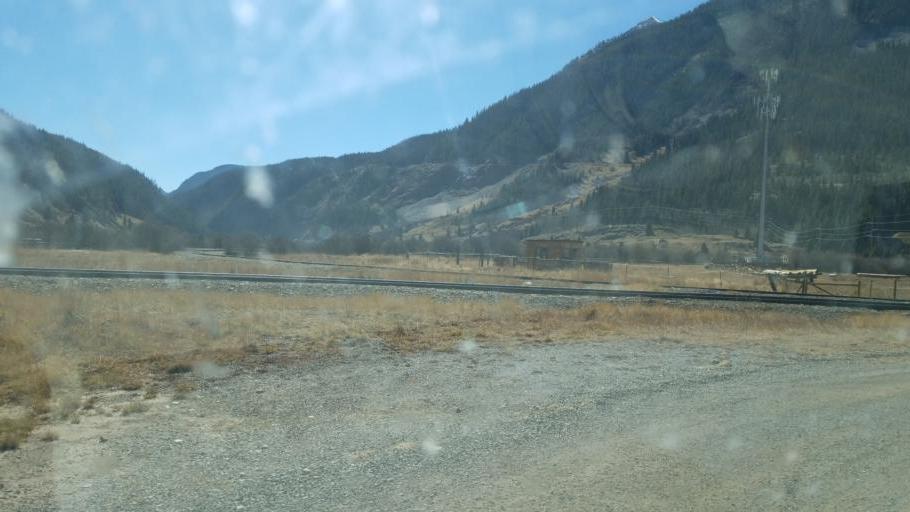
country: US
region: Colorado
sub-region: San Juan County
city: Silverton
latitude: 37.8044
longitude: -107.6671
